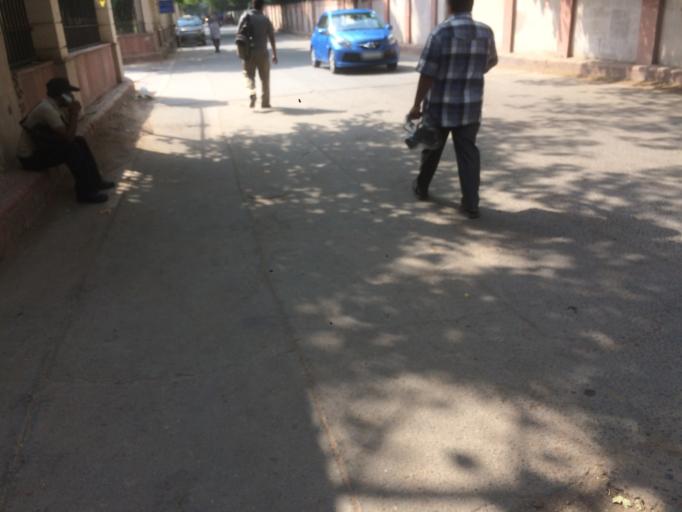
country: IN
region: NCT
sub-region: New Delhi
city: New Delhi
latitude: 28.6366
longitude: 77.2162
